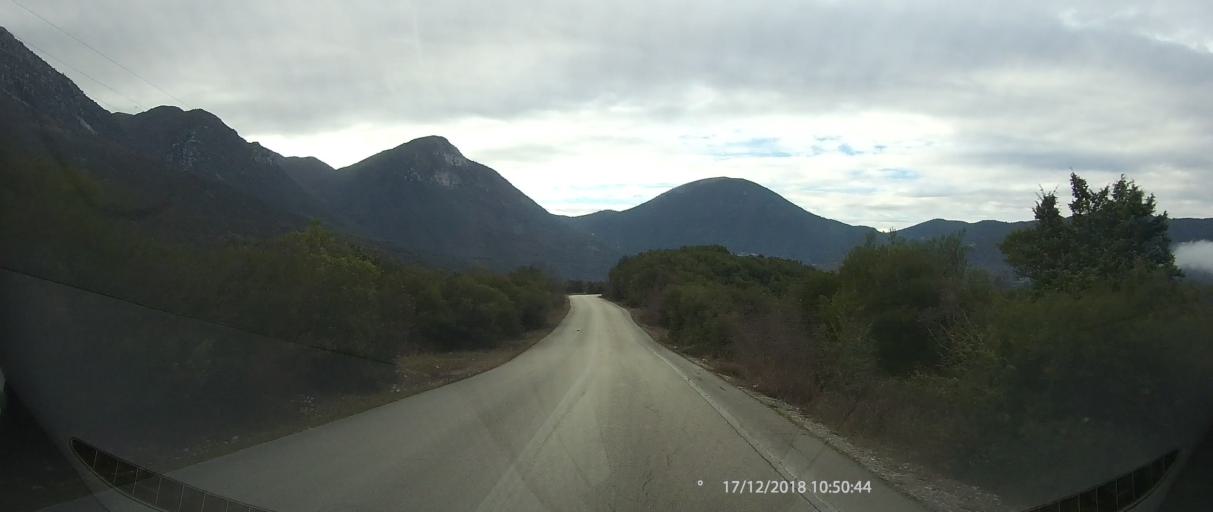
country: GR
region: Epirus
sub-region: Nomos Ioanninon
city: Kalpaki
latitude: 39.9548
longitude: 20.6959
